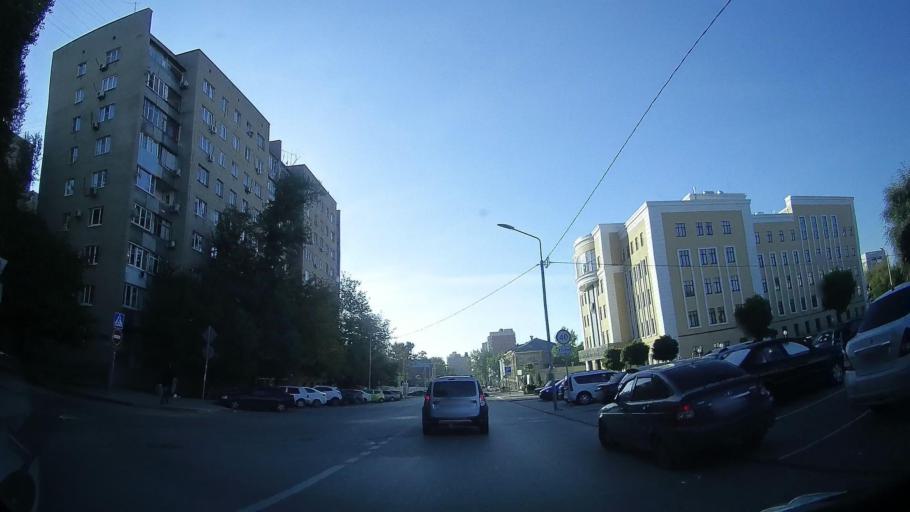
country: RU
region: Rostov
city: Rostov-na-Donu
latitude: 47.2278
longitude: 39.6986
